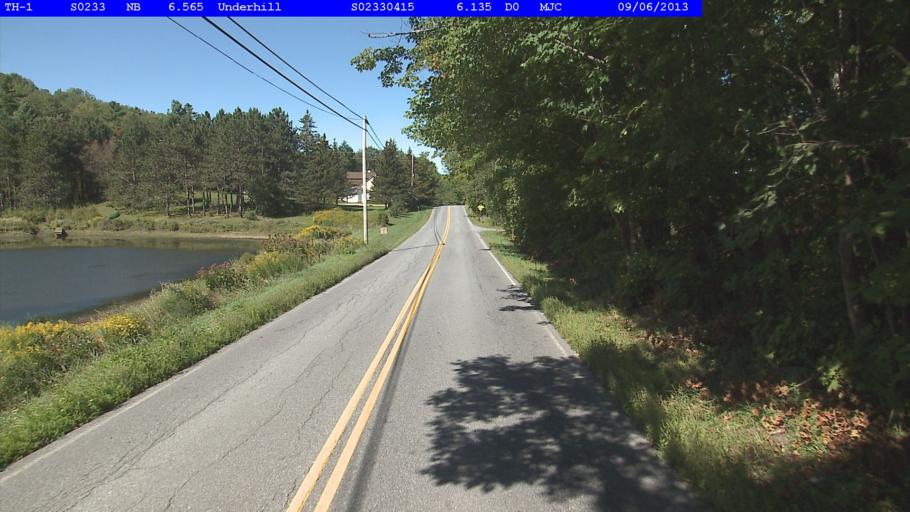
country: US
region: Vermont
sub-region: Chittenden County
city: Jericho
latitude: 44.5533
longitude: -72.8671
